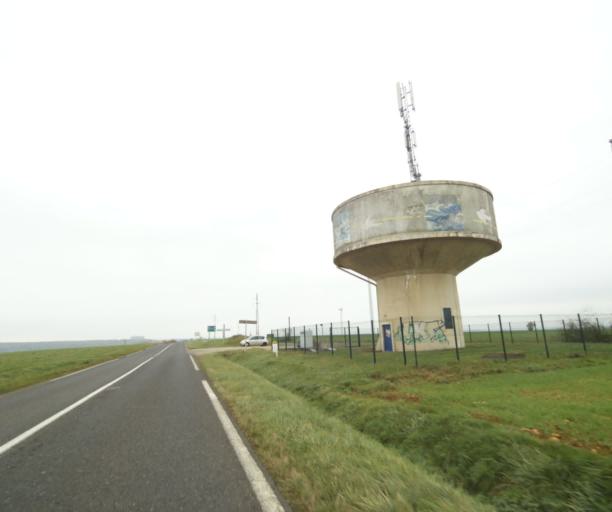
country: FR
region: Lorraine
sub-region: Departement de Meurthe-et-Moselle
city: Mancieulles
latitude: 49.2720
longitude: 5.8913
